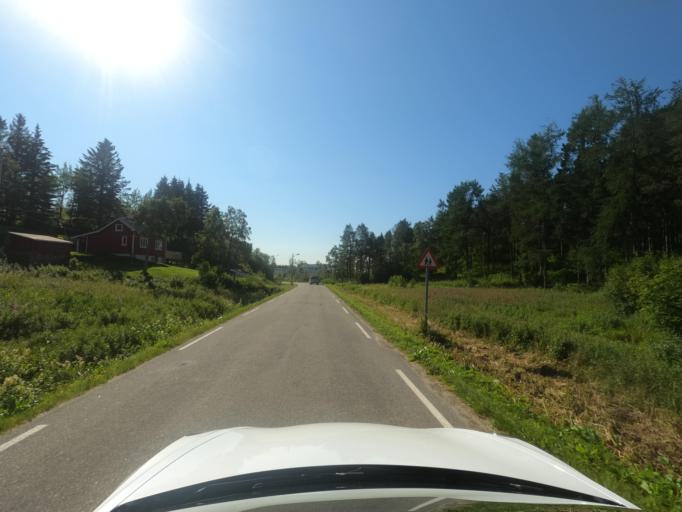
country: NO
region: Nordland
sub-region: Hadsel
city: Stokmarknes
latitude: 68.3123
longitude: 14.9870
